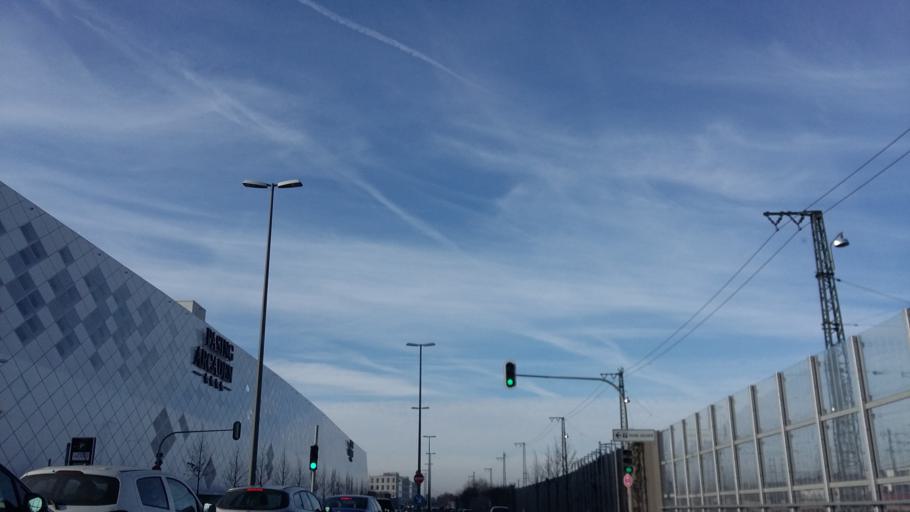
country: DE
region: Bavaria
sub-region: Upper Bavaria
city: Pasing
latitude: 48.1482
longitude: 11.4661
